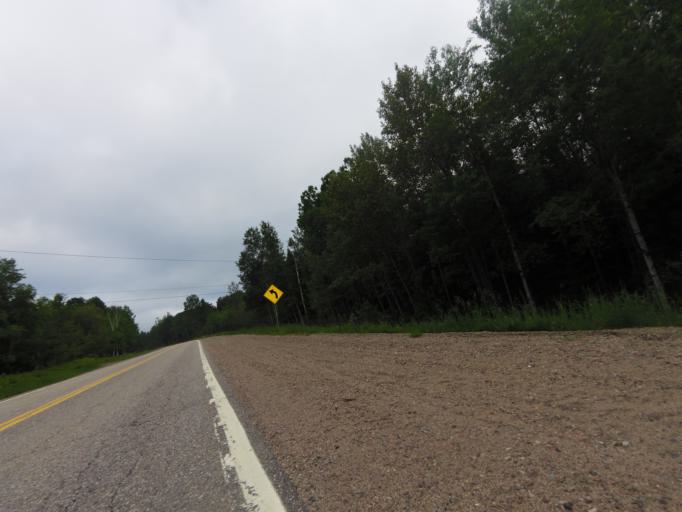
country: CA
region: Quebec
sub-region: Outaouais
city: Shawville
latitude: 45.9104
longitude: -76.3135
